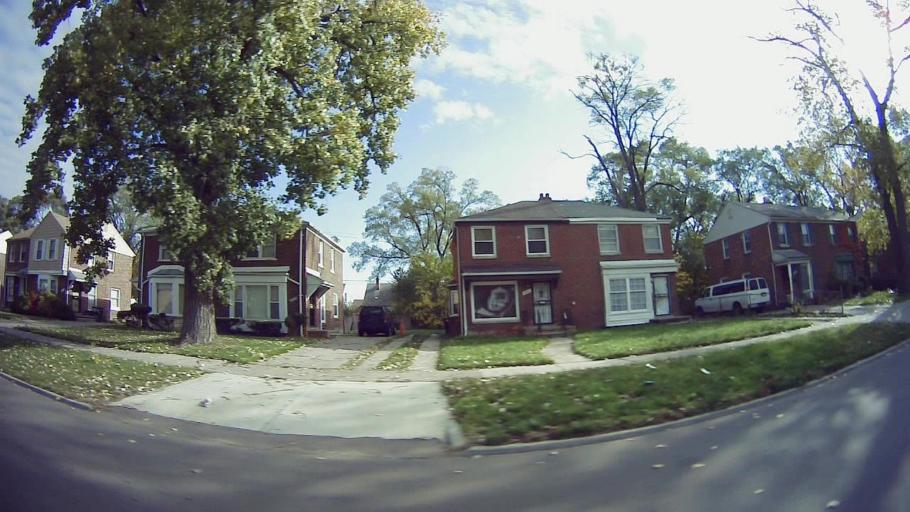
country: US
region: Michigan
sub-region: Oakland County
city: Oak Park
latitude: 42.4391
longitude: -83.1807
